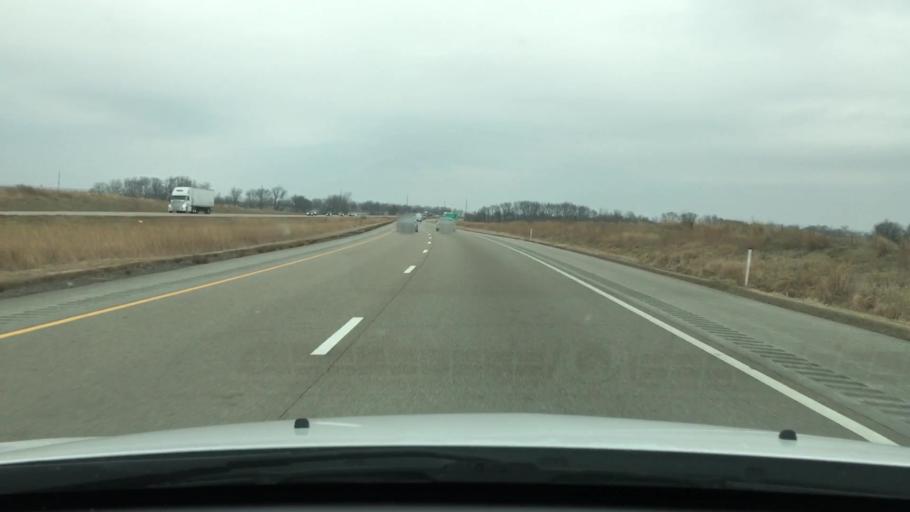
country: US
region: Illinois
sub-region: Logan County
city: Atlanta
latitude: 40.2693
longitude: -89.2128
